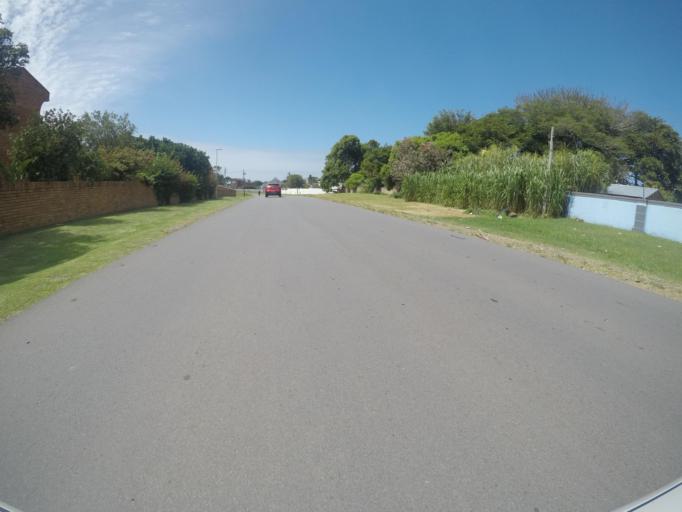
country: ZA
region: Eastern Cape
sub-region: Buffalo City Metropolitan Municipality
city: East London
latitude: -32.9526
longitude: 27.9980
